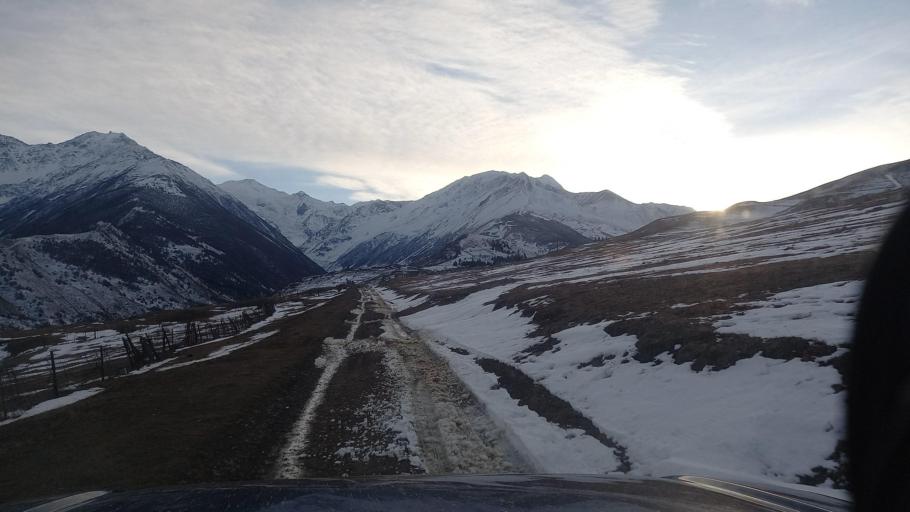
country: RU
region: Ingushetiya
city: Dzhayrakh
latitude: 42.8535
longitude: 44.5153
